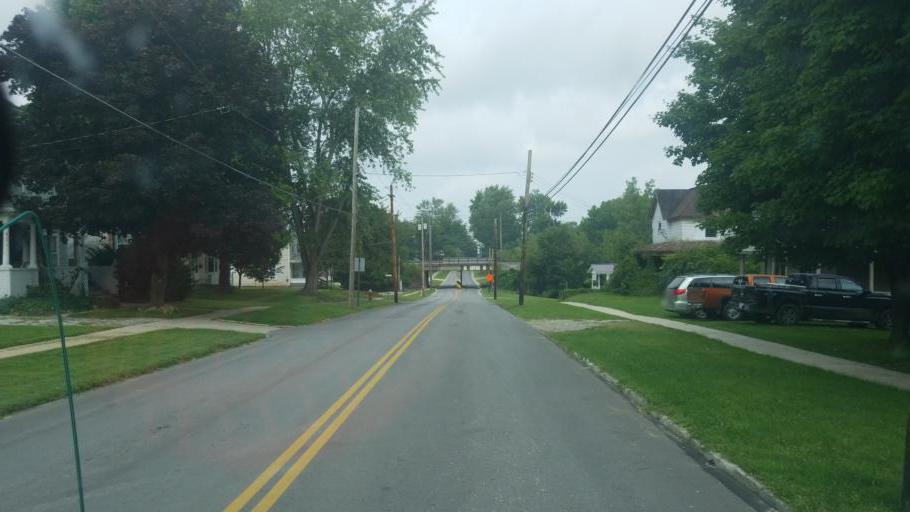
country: US
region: Ohio
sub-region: Huron County
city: Greenwich
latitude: 41.0336
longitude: -82.5165
